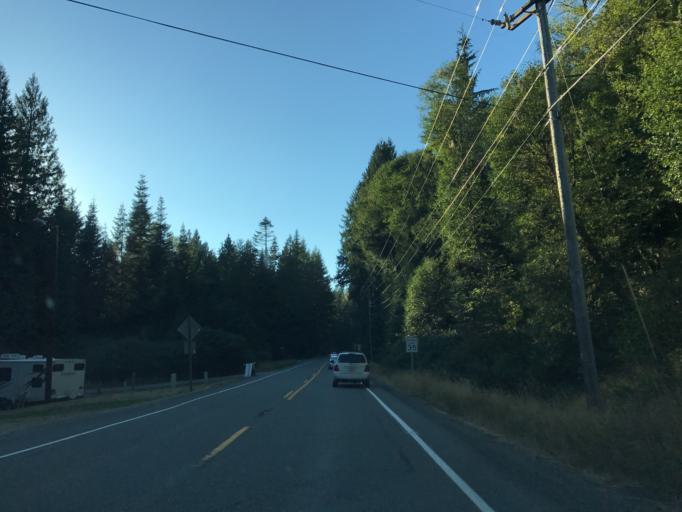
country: US
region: Washington
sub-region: Pierce County
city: Eatonville
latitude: 46.7419
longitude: -121.9201
